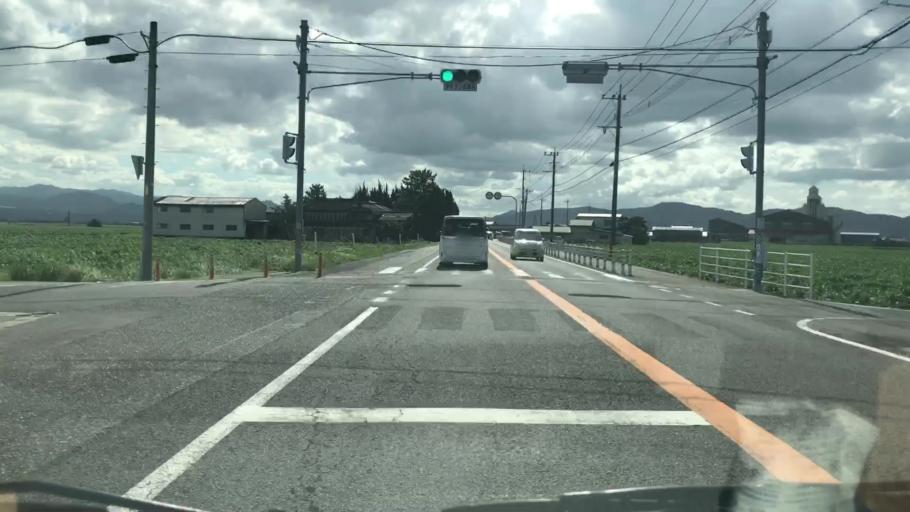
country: JP
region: Saga Prefecture
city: Kashima
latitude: 33.1676
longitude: 130.1760
